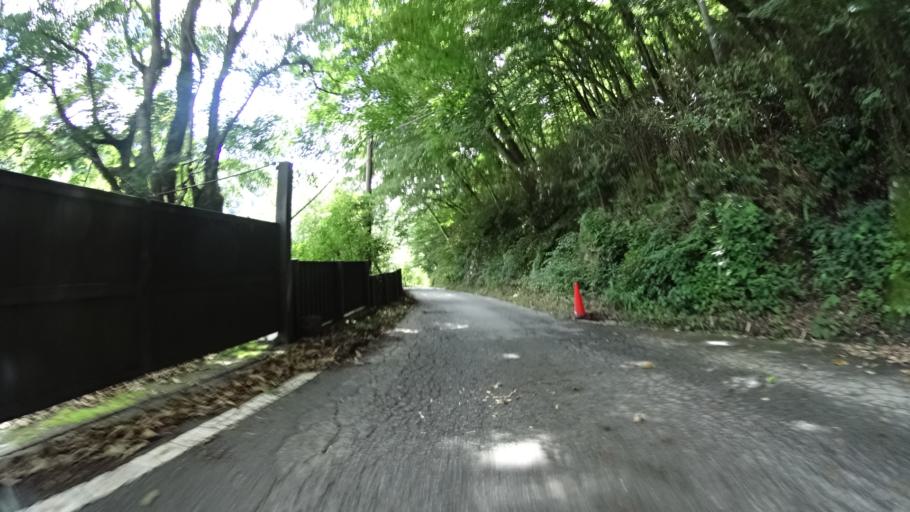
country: JP
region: Yamanashi
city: Enzan
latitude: 35.6843
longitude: 138.8110
